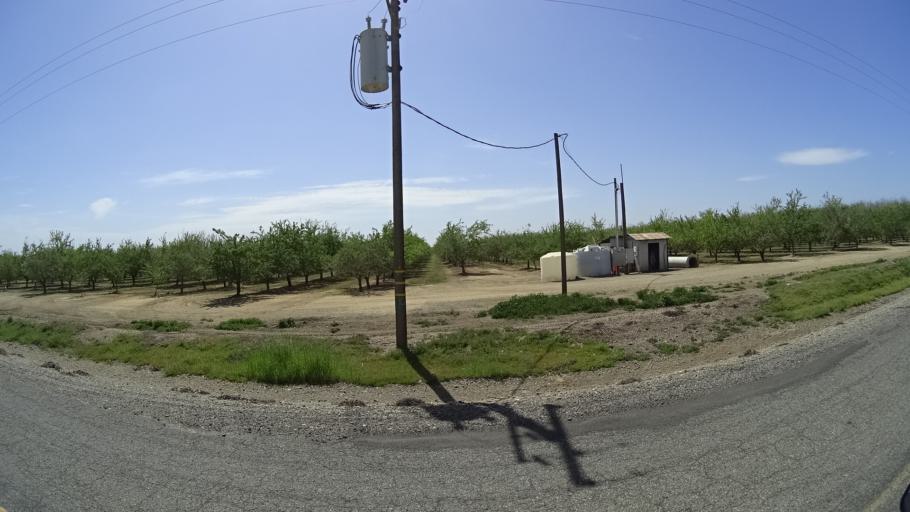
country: US
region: California
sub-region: Glenn County
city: Hamilton City
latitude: 39.6524
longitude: -122.0945
